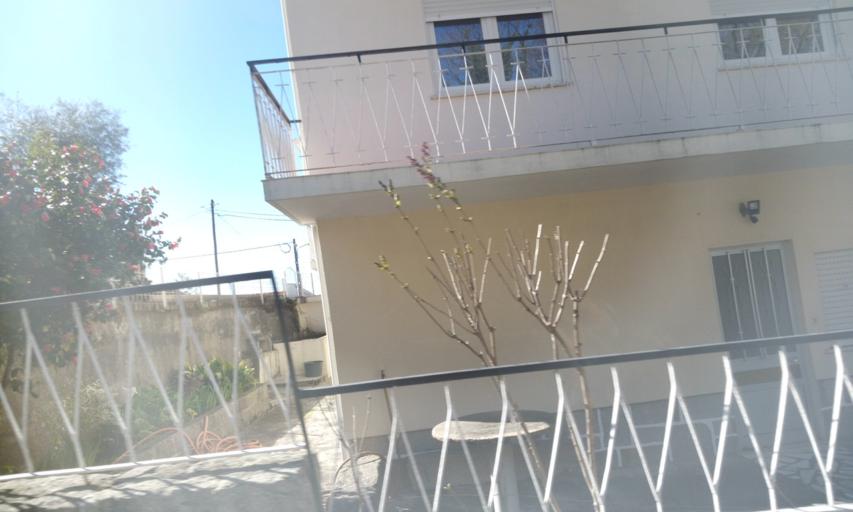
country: PT
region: Guarda
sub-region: Manteigas
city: Manteigas
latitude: 40.4922
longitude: -7.5885
